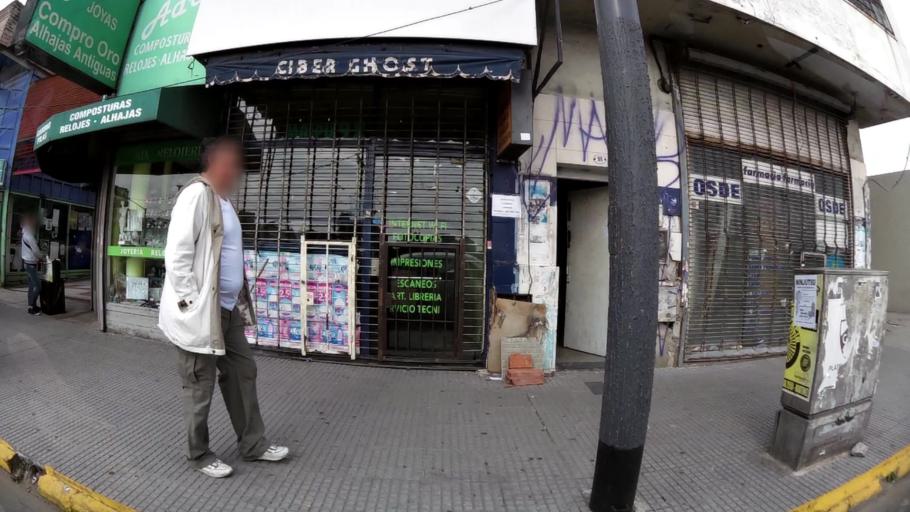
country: AR
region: Buenos Aires
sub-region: Partido de Vicente Lopez
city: Olivos
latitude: -34.5371
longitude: -58.4767
